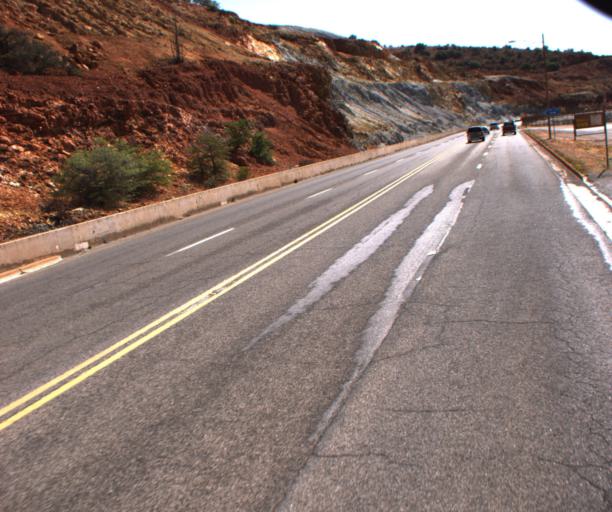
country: US
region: Arizona
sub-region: Cochise County
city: Bisbee
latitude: 31.4362
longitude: -109.9010
